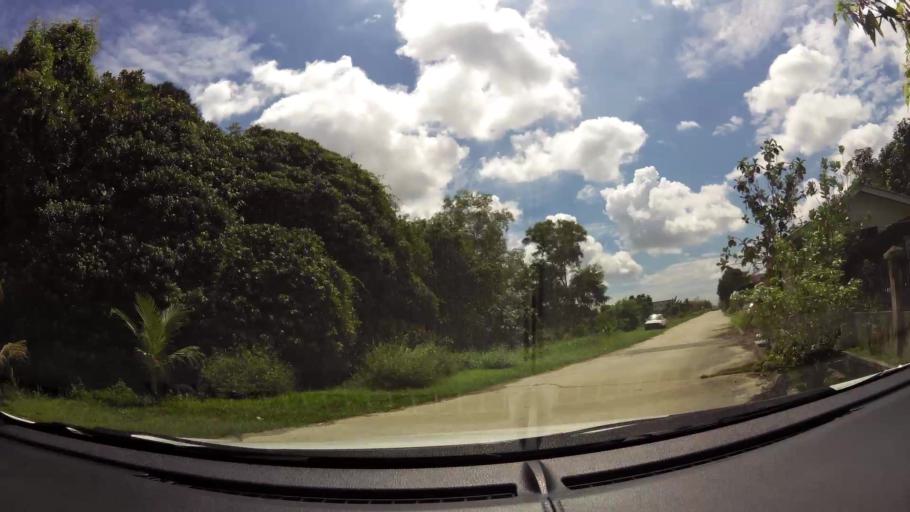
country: BN
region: Brunei and Muara
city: Bandar Seri Begawan
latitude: 4.9431
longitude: 114.9019
